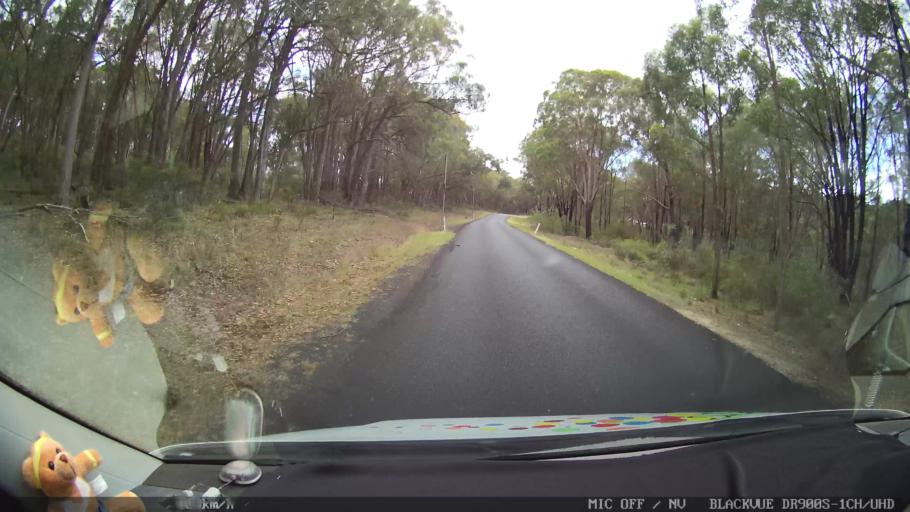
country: AU
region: New South Wales
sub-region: Glen Innes Severn
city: Glen Innes
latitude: -29.4338
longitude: 151.6329
